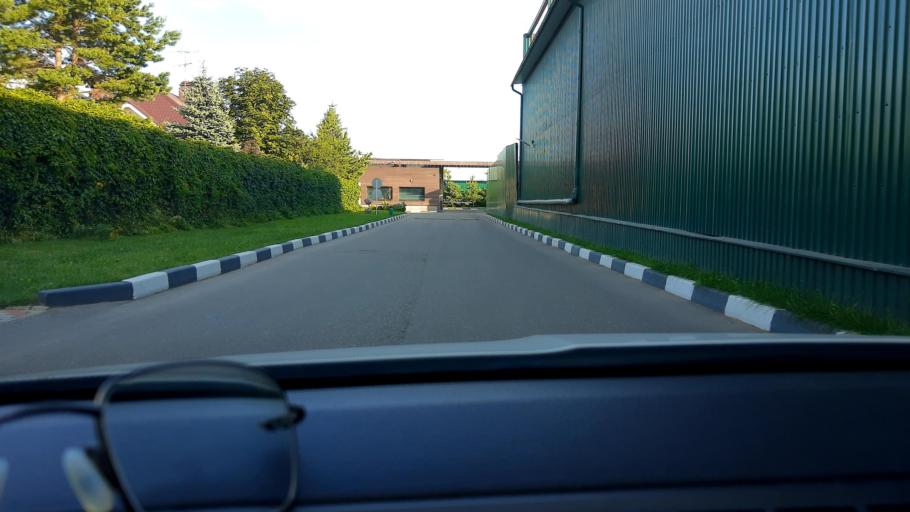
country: RU
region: Moskovskaya
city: Opalikha
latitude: 55.7776
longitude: 37.2435
